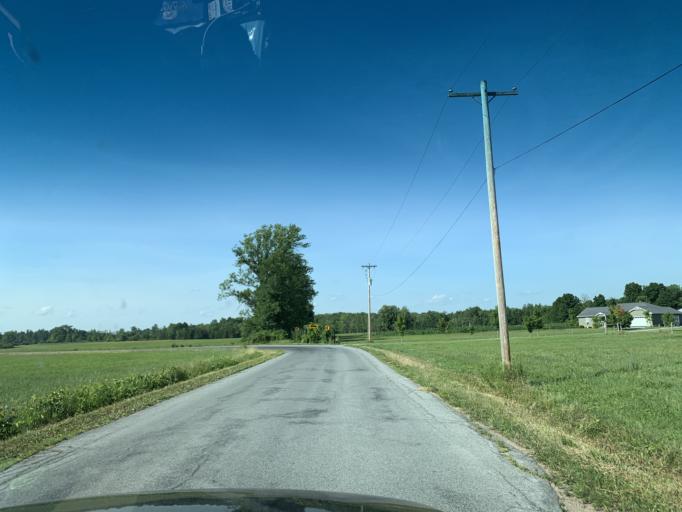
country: US
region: New York
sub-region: Madison County
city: Oneida
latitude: 43.1473
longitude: -75.6580
